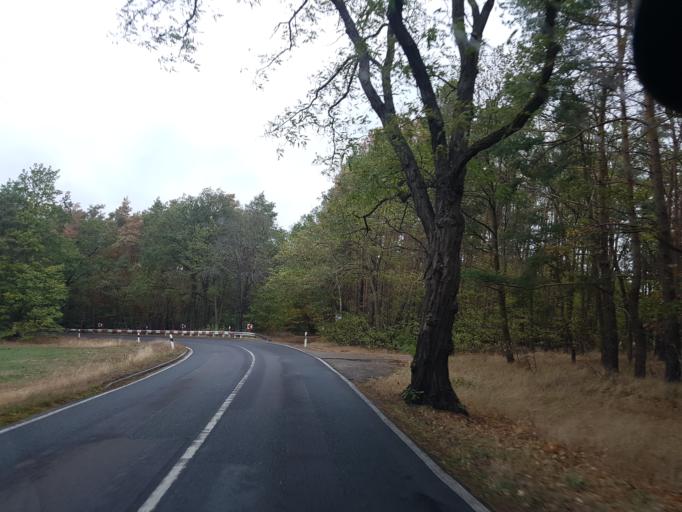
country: DE
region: Brandenburg
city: Falkenberg
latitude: 51.6122
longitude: 13.2388
